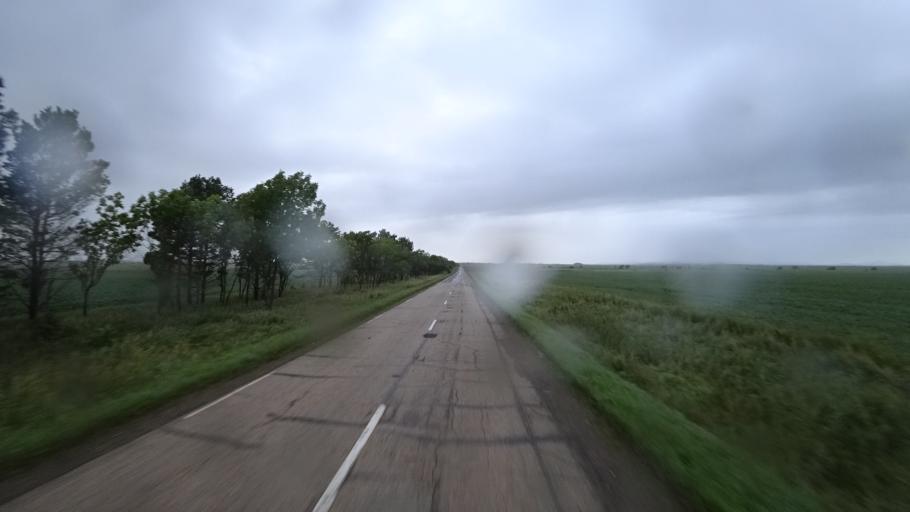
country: RU
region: Primorskiy
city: Chernigovka
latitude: 44.3755
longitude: 132.5297
